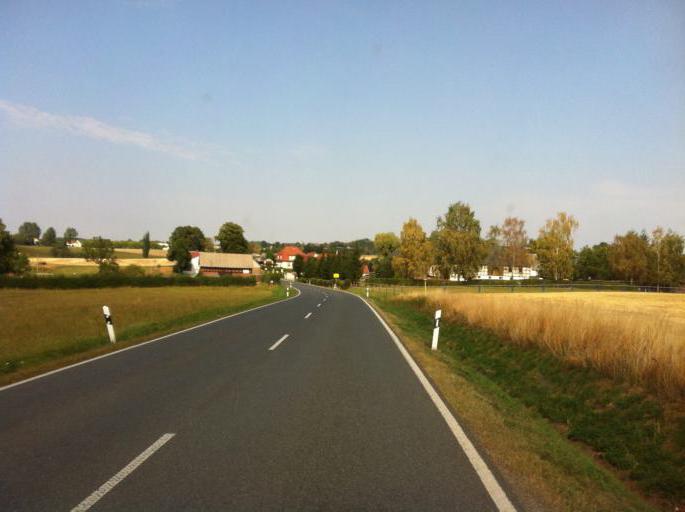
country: DE
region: Saxony
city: Neumark
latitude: 50.6606
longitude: 12.3695
